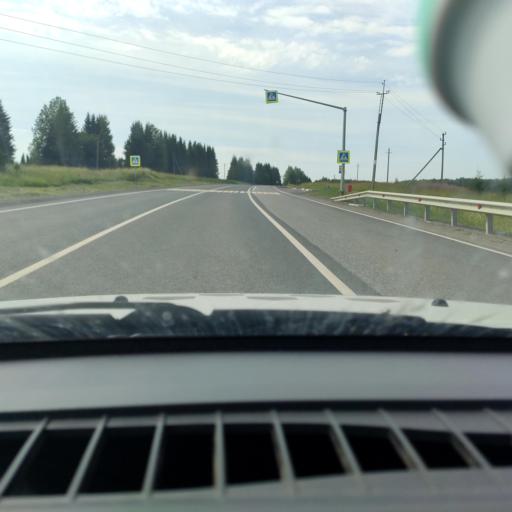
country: RU
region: Perm
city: Siva
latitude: 58.4852
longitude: 54.0731
